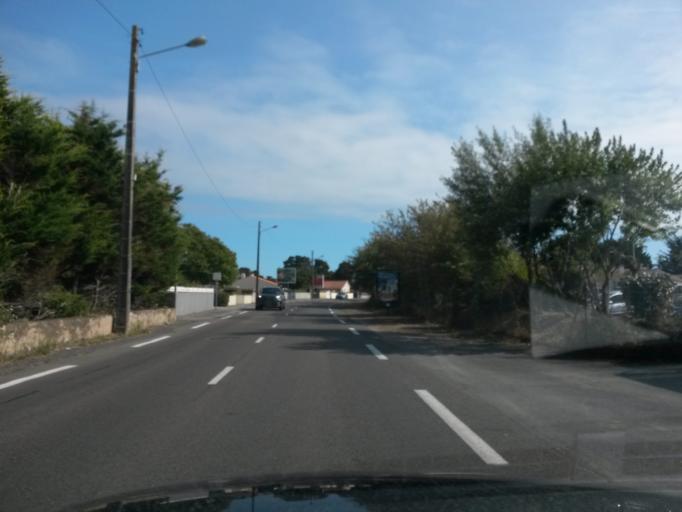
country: FR
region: Pays de la Loire
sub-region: Departement de la Vendee
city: Olonne-sur-Mer
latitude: 46.5527
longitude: -1.8072
